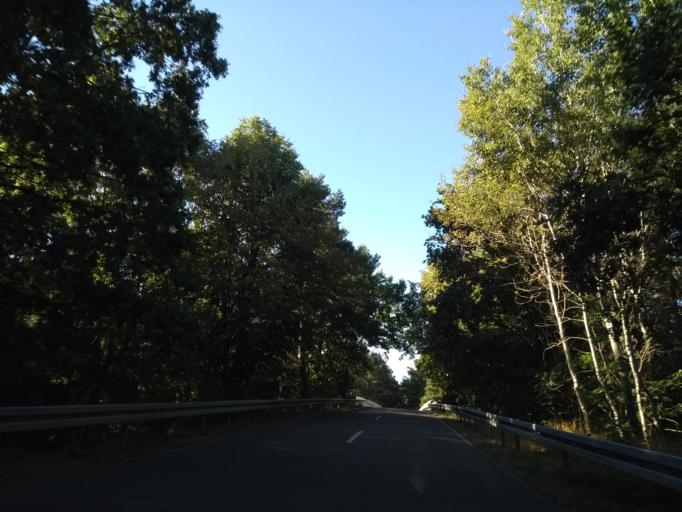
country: DE
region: Brandenburg
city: Lubbenau
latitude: 51.8405
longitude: 13.9508
